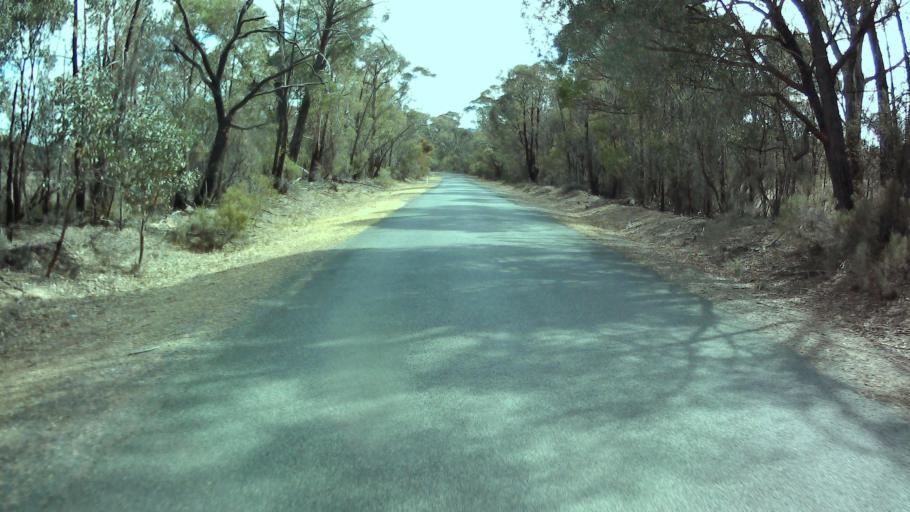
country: AU
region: New South Wales
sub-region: Weddin
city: Grenfell
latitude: -33.8711
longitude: 148.2031
